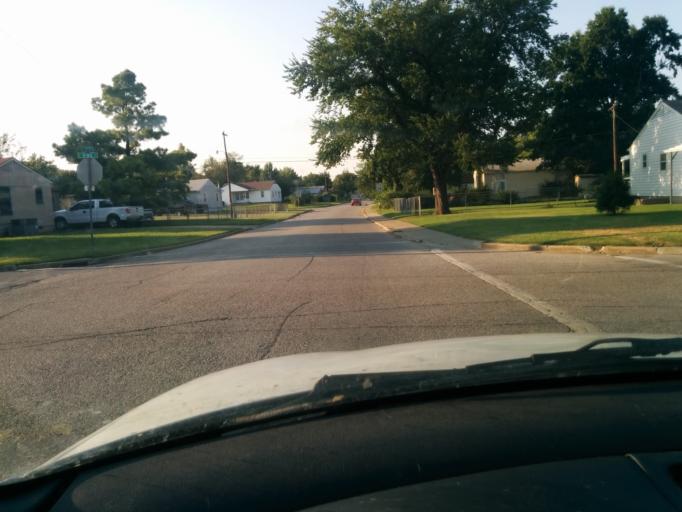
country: US
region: Oklahoma
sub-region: Tulsa County
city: Tulsa
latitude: 36.1684
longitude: -95.8955
